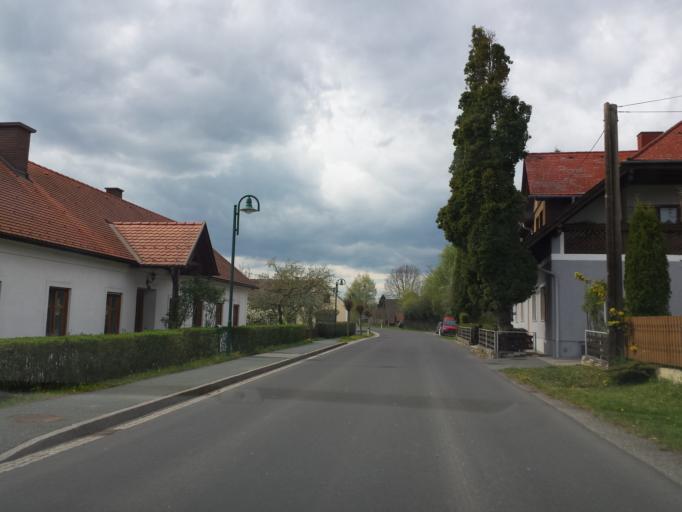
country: AT
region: Styria
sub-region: Politischer Bezirk Hartberg-Fuerstenfeld
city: Loipersdorf bei Fuerstenfeld
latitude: 47.0175
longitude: 16.1064
